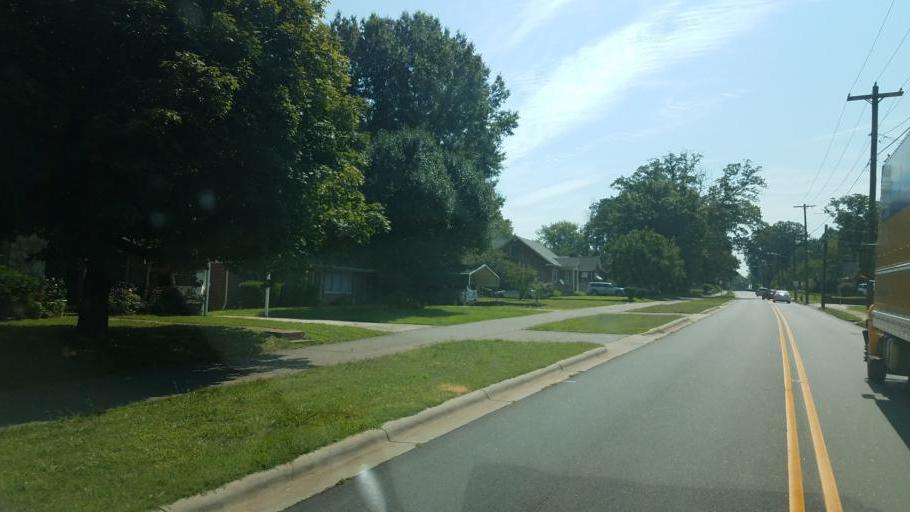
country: US
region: North Carolina
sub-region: Burke County
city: Morganton
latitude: 35.7486
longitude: -81.6967
